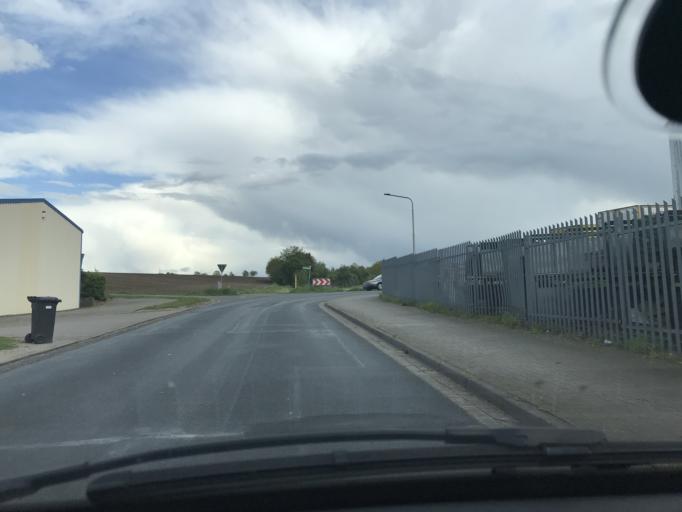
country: DE
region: Lower Saxony
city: Harsefeld
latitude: 53.4623
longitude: 9.5239
